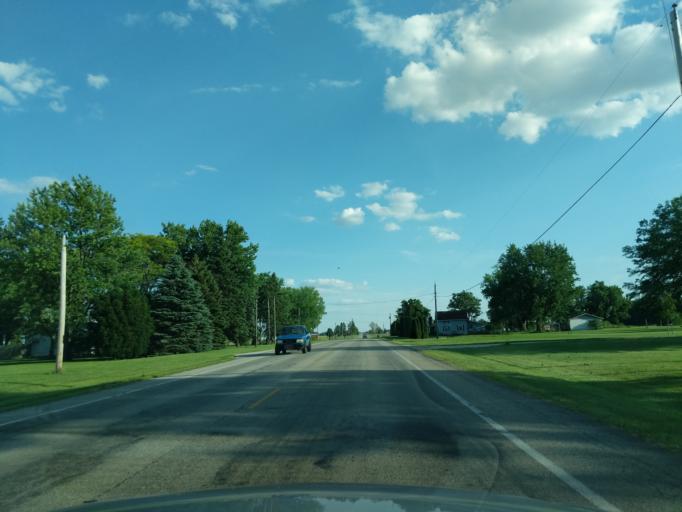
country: US
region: Indiana
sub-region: Whitley County
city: Columbia City
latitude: 41.0705
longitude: -85.4703
